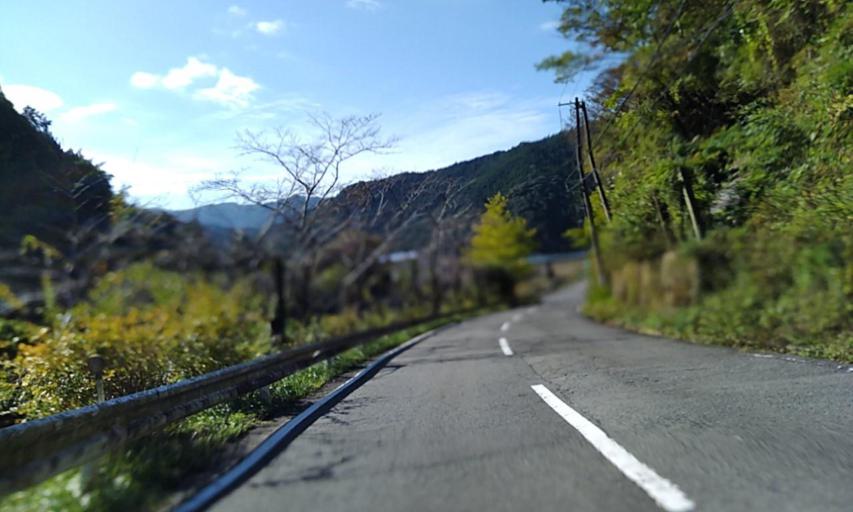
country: JP
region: Wakayama
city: Kainan
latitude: 34.0737
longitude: 135.3578
